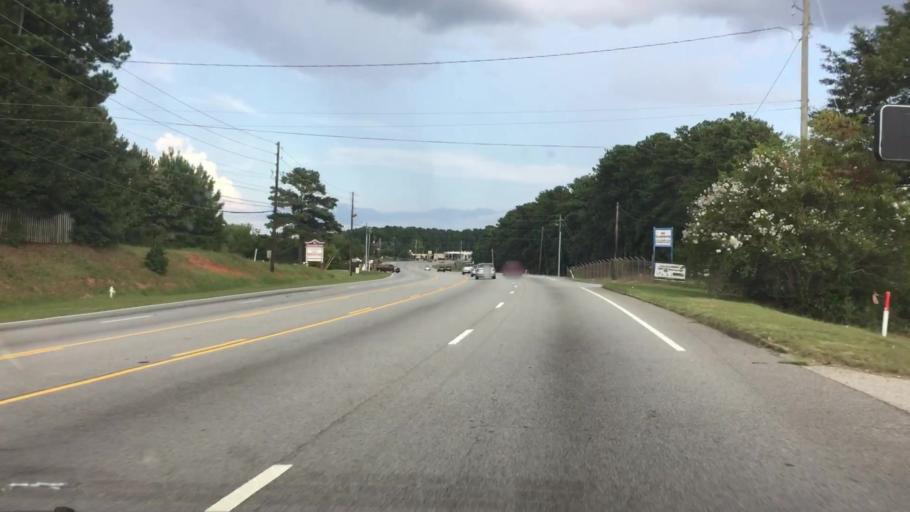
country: US
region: Georgia
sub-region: Clayton County
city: Riverdale
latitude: 33.5474
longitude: -84.4104
